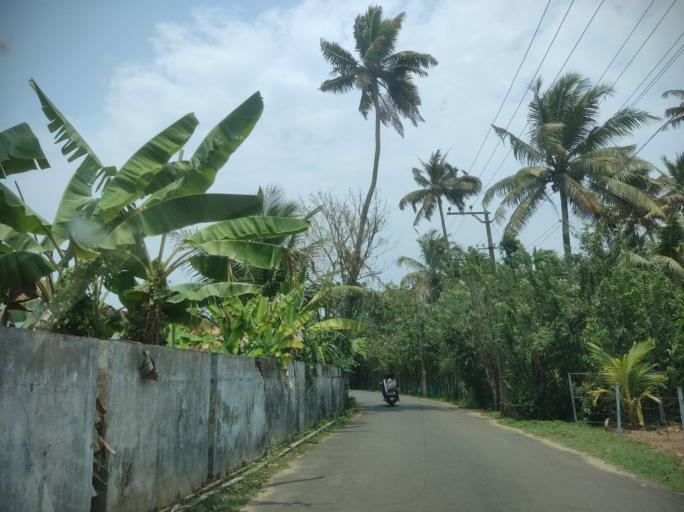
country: IN
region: Kerala
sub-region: Alappuzha
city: Vayalar
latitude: 9.7422
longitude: 76.3258
